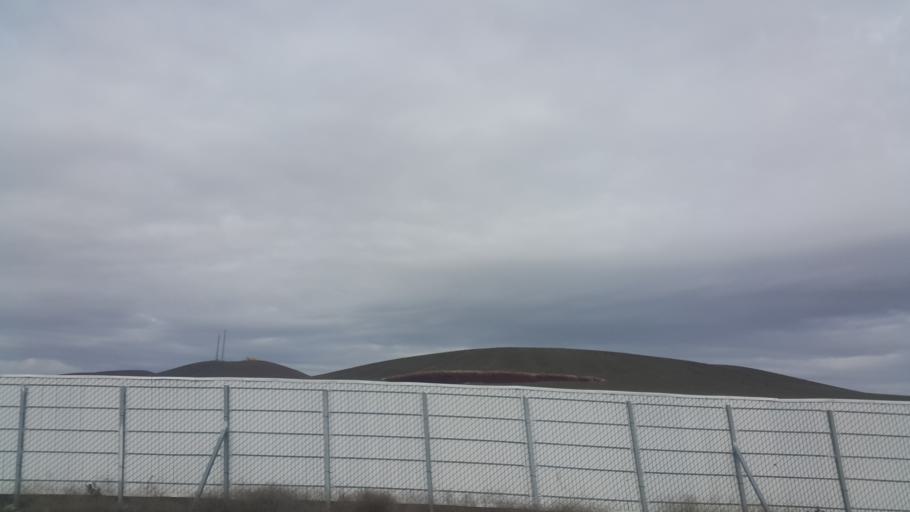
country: TR
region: Aksaray
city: Taspinar
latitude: 37.9421
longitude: 34.0956
